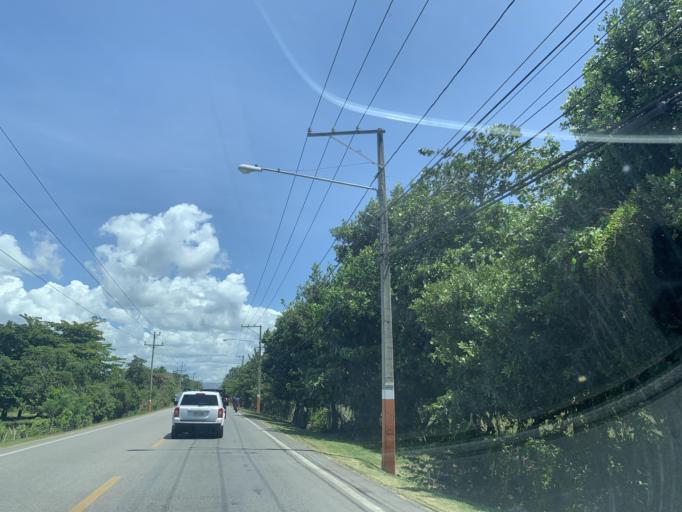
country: DO
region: Puerto Plata
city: Cabarete
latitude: 19.7311
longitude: -70.3885
